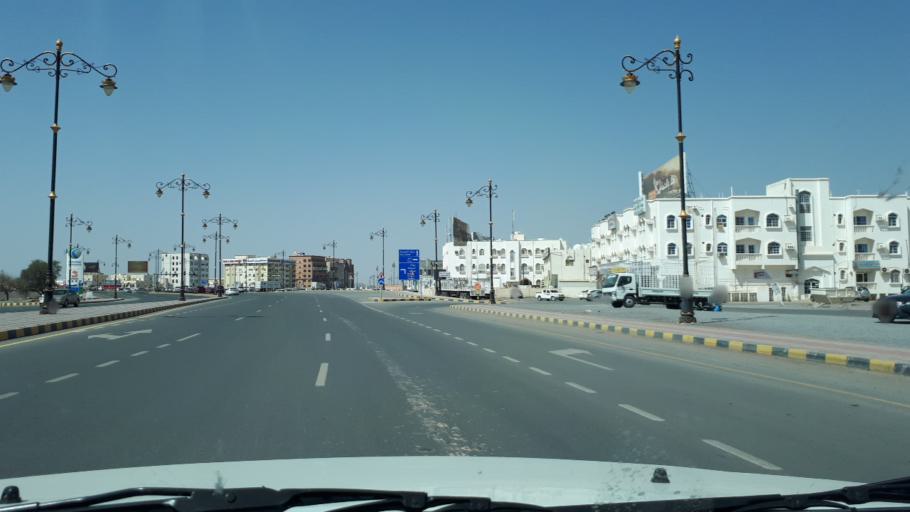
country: OM
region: Muhafazat ad Dakhiliyah
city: Nizwa
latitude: 22.8774
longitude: 57.5353
